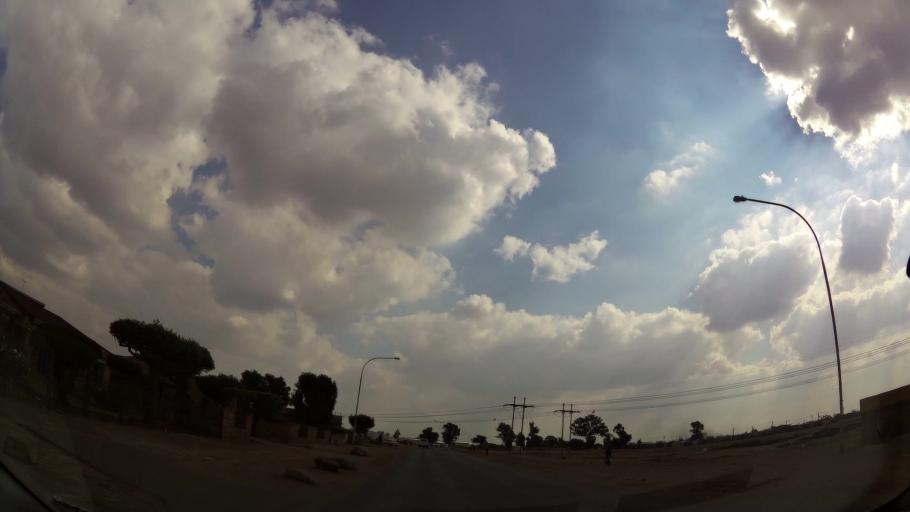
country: ZA
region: Gauteng
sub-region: Ekurhuleni Metropolitan Municipality
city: Benoni
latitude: -26.1365
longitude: 28.4182
